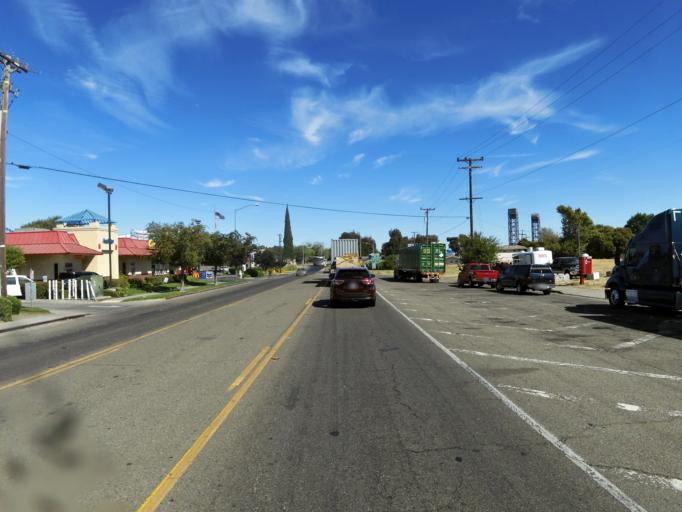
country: US
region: California
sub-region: Solano County
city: Rio Vista
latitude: 38.1607
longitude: -121.6913
